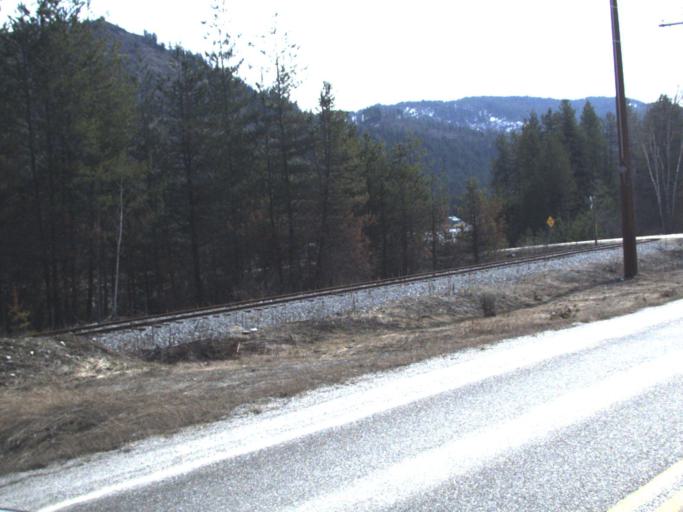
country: US
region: Washington
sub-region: Stevens County
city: Chewelah
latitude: 48.6466
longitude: -117.3780
